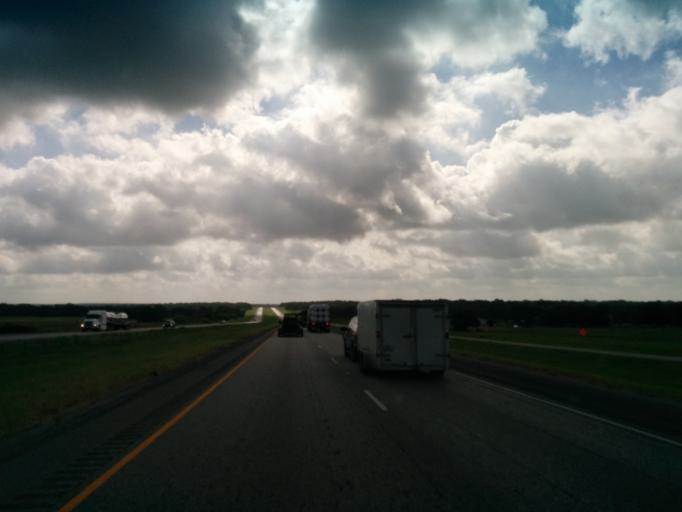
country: US
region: Texas
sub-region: Gonzales County
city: Waelder
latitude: 29.6584
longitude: -97.4132
